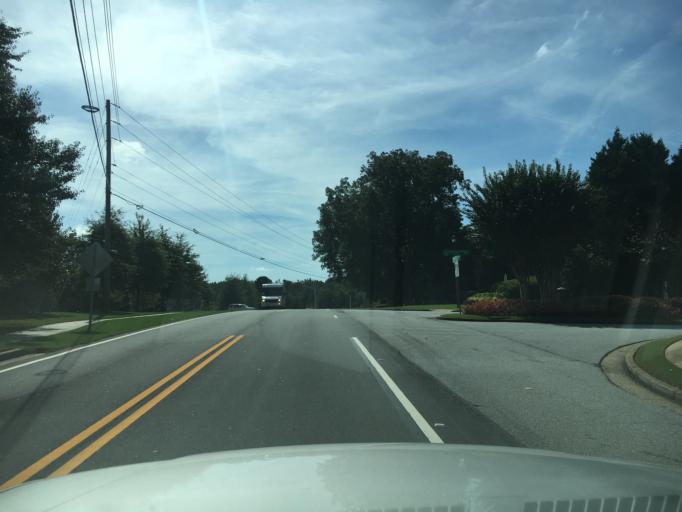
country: US
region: Georgia
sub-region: Gwinnett County
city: Duluth
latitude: 33.9867
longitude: -84.1006
